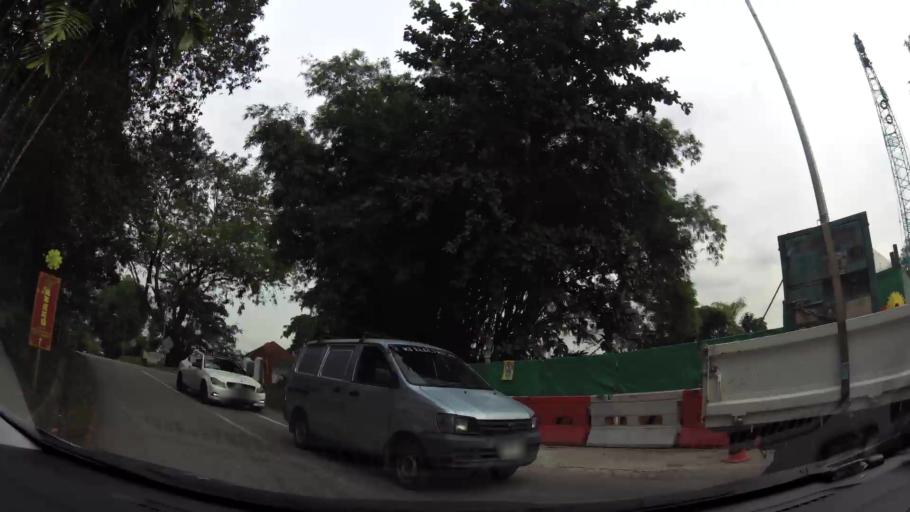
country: MY
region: Johor
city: Kampung Pasir Gudang Baru
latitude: 1.4197
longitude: 103.8248
